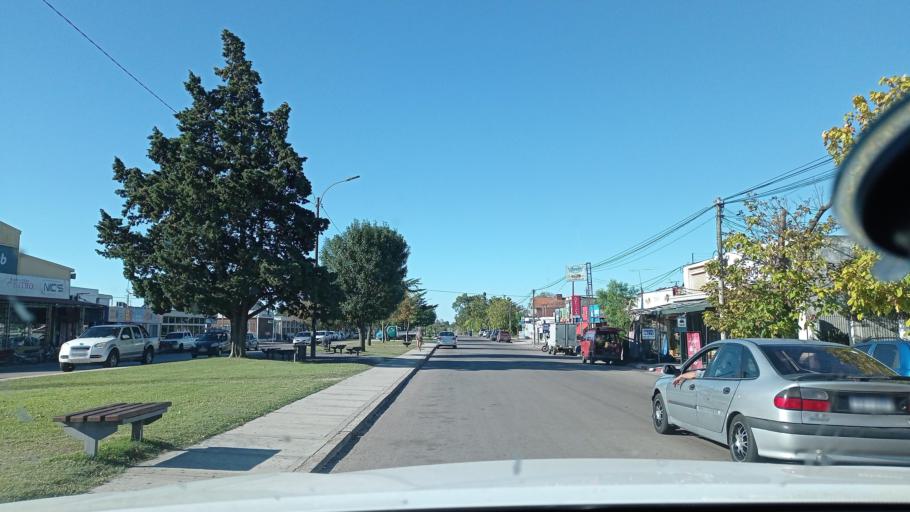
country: UY
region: Canelones
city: San Jacinto
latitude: -34.5456
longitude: -55.8709
